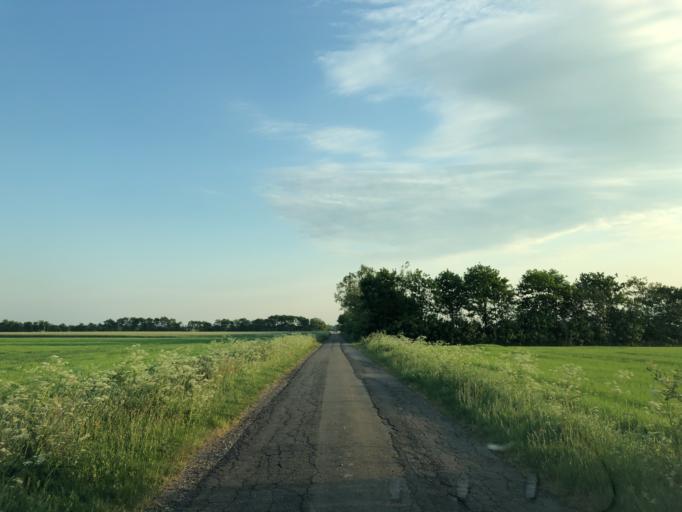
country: DK
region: Central Jutland
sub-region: Holstebro Kommune
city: Holstebro
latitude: 56.3858
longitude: 8.4695
